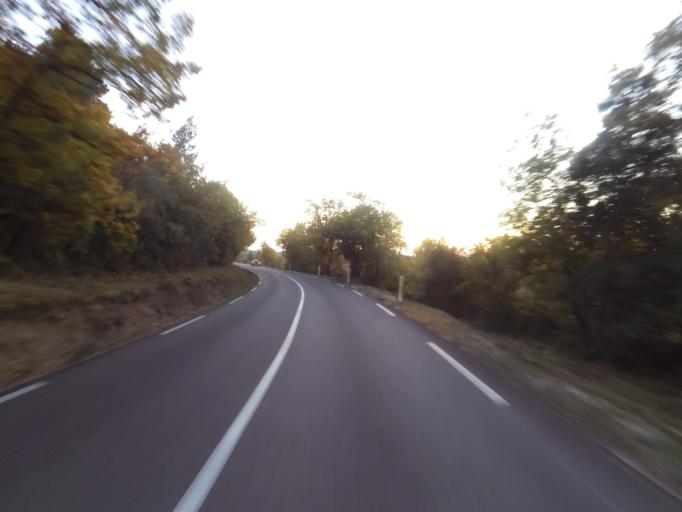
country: FR
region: Provence-Alpes-Cote d'Azur
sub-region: Departement du Vaucluse
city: Caromb
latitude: 44.1006
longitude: 5.1438
